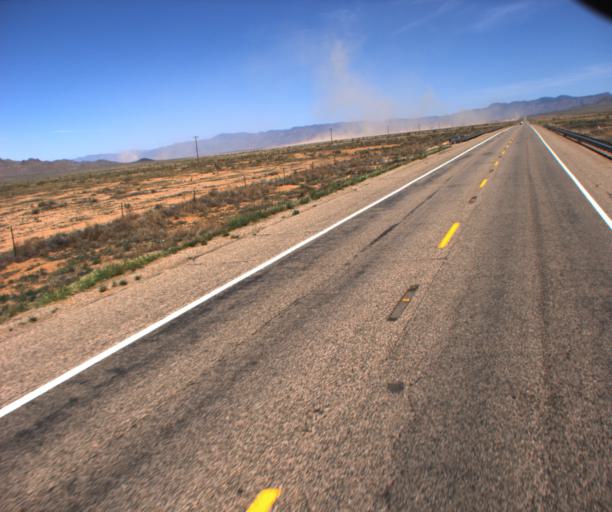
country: US
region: Arizona
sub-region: Mohave County
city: New Kingman-Butler
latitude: 35.3147
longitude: -113.9175
